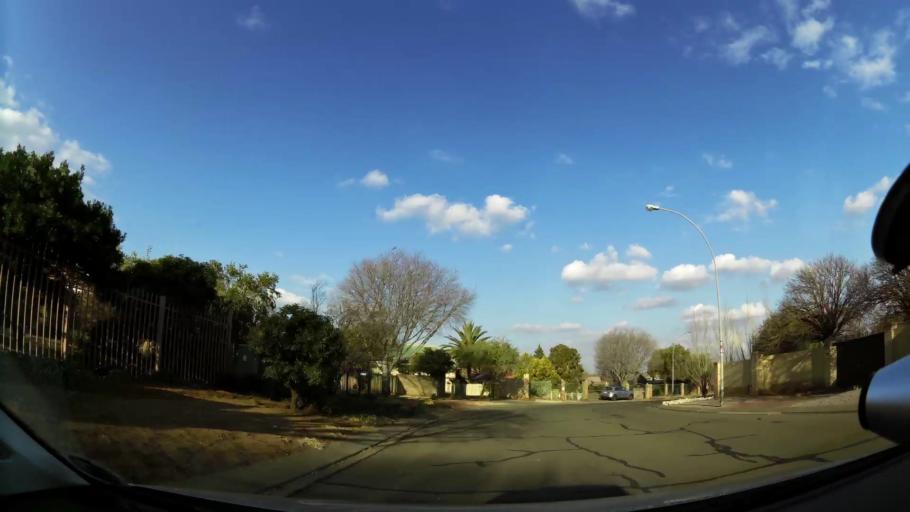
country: ZA
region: Orange Free State
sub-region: Mangaung Metropolitan Municipality
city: Bloemfontein
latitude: -29.1556
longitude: 26.1823
